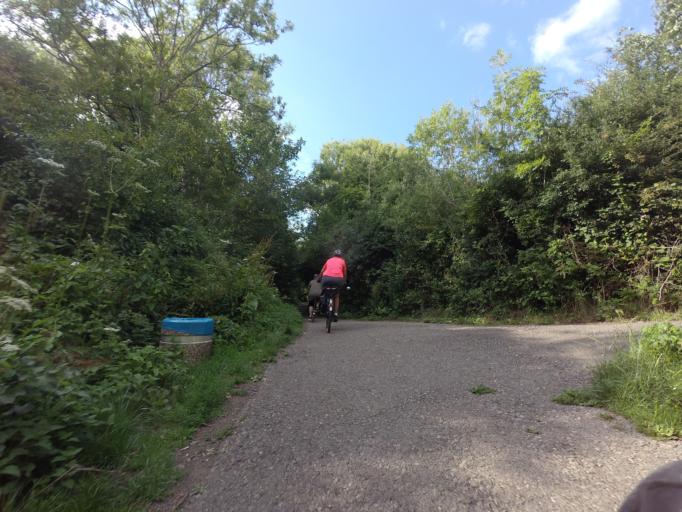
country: GB
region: England
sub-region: East Sussex
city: Hailsham
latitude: 50.8646
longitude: 0.2554
